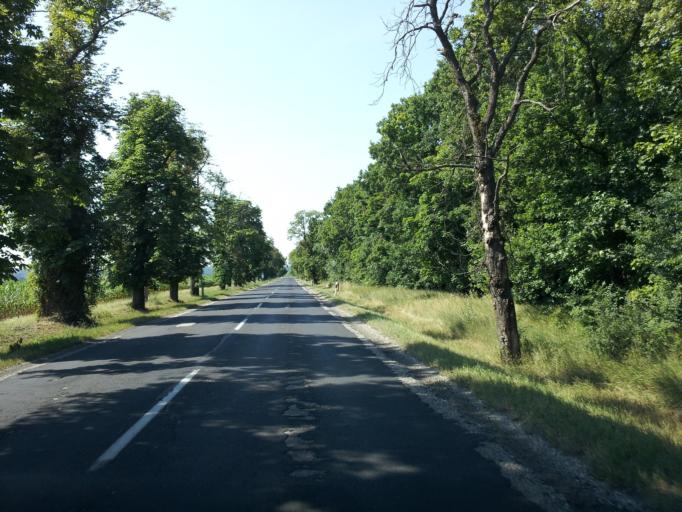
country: HU
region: Fejer
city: Lovasbereny
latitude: 47.3045
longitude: 18.5383
